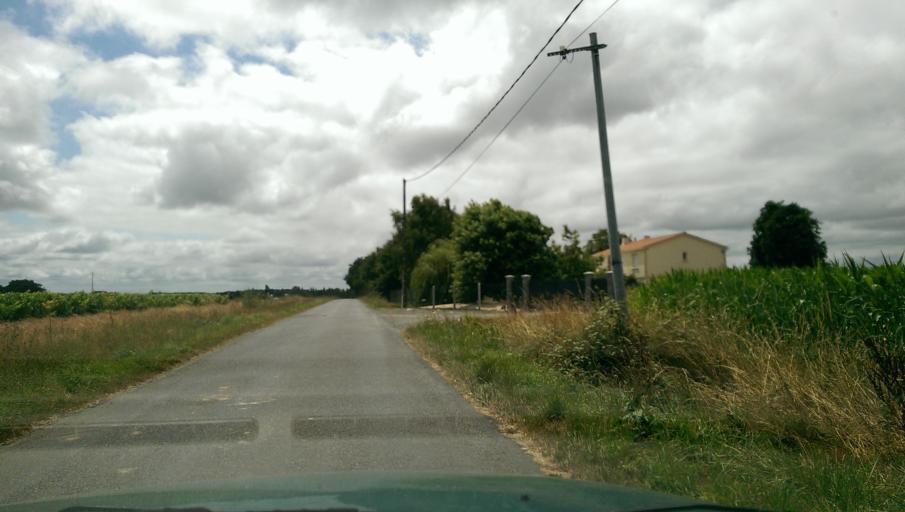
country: FR
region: Pays de la Loire
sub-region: Departement de la Loire-Atlantique
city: Remouille
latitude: 47.0638
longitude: -1.3631
